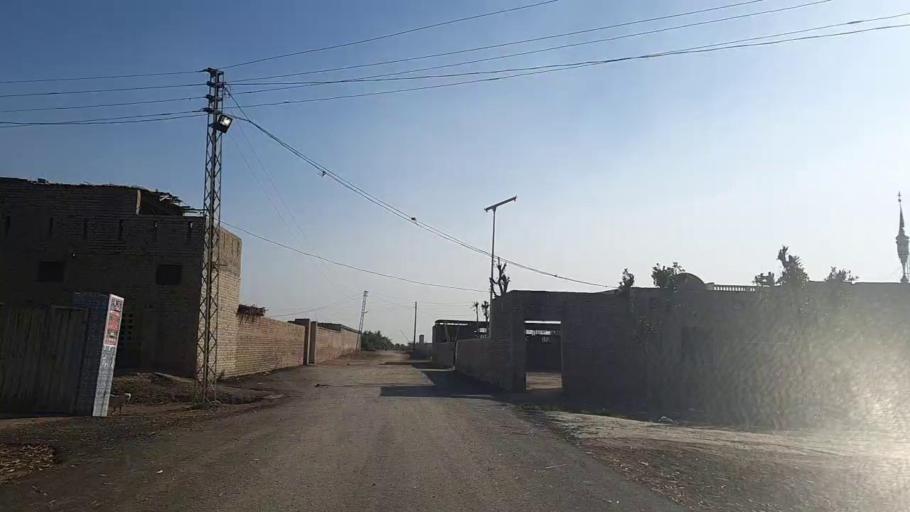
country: PK
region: Sindh
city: Shahpur Chakar
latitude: 26.2162
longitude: 68.6424
